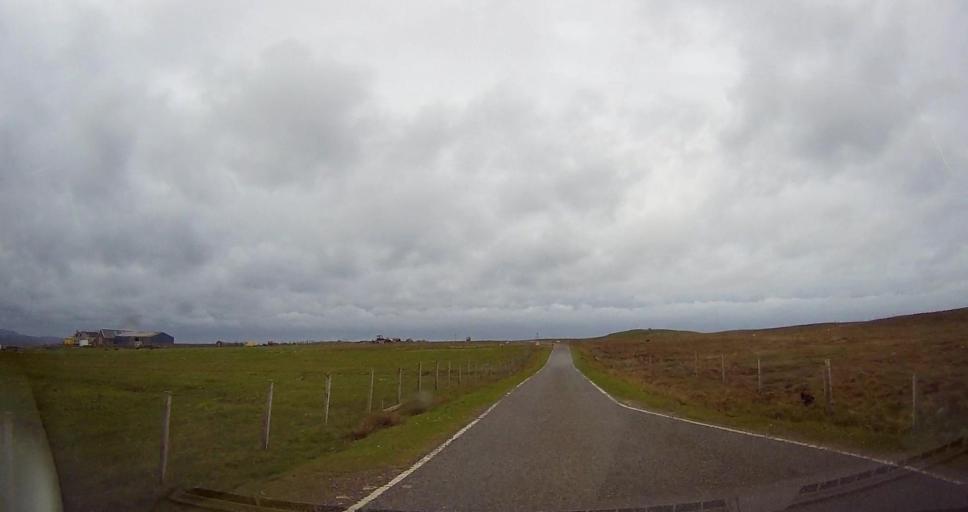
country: GB
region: Scotland
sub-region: Shetland Islands
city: Lerwick
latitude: 60.4889
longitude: -1.5971
